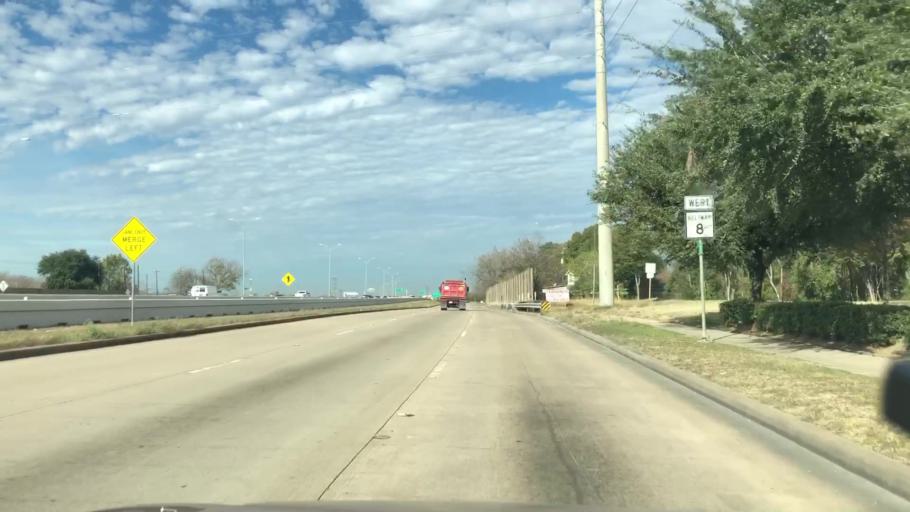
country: US
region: Texas
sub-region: Fort Bend County
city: Missouri City
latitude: 29.6163
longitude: -95.4982
